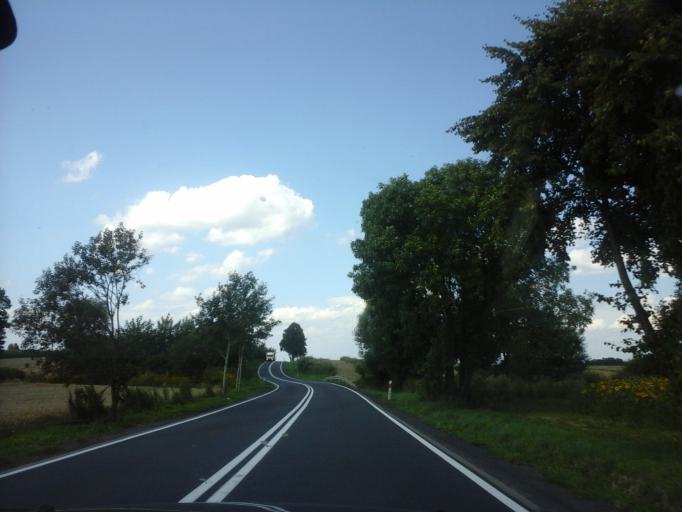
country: PL
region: Lesser Poland Voivodeship
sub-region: Powiat wadowicki
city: Spytkowice
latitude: 49.9892
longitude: 19.5230
